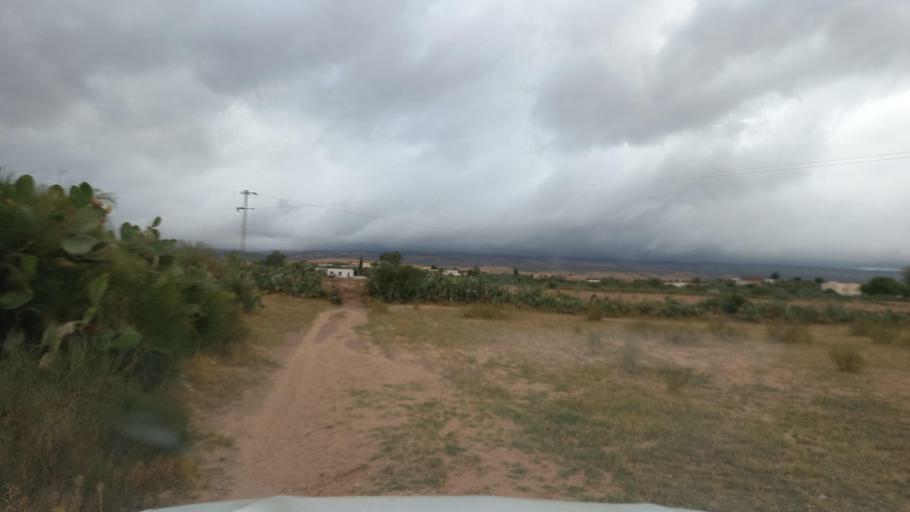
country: TN
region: Al Qasrayn
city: Kasserine
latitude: 35.2768
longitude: 8.9468
